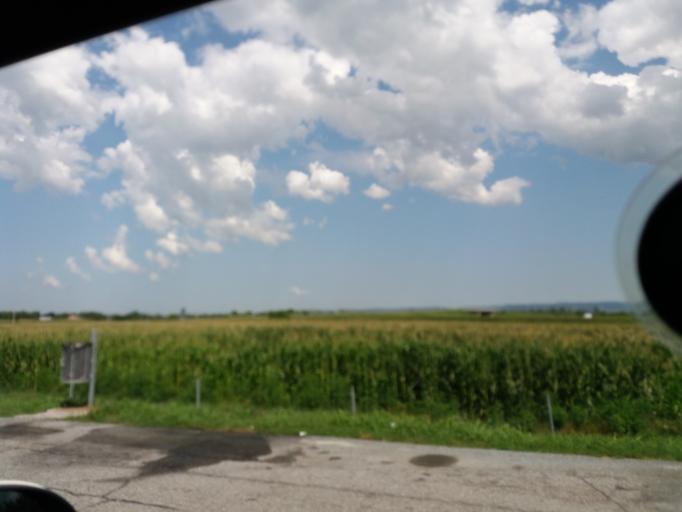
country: RS
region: Autonomna Pokrajina Vojvodina
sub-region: Sremski Okrug
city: Sremska Mitrovica
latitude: 44.9954
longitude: 19.6437
